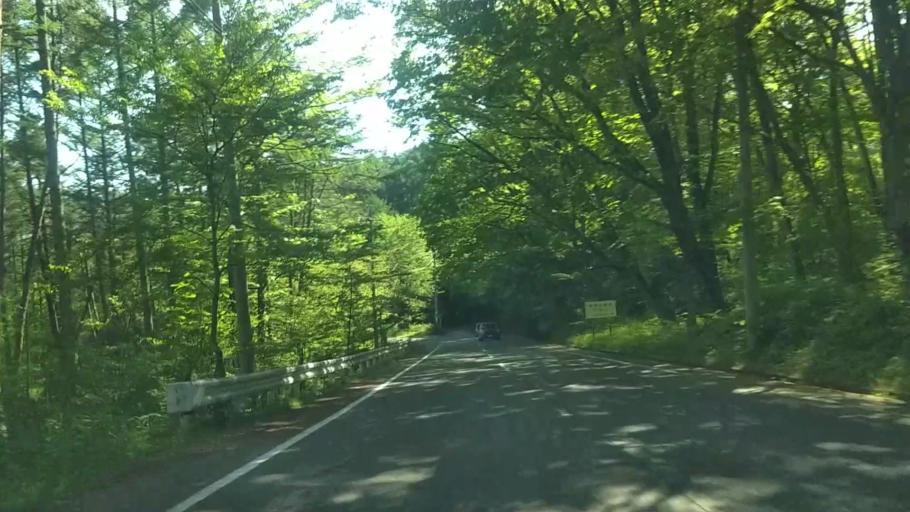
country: JP
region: Yamanashi
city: Nirasaki
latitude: 35.8877
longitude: 138.3894
